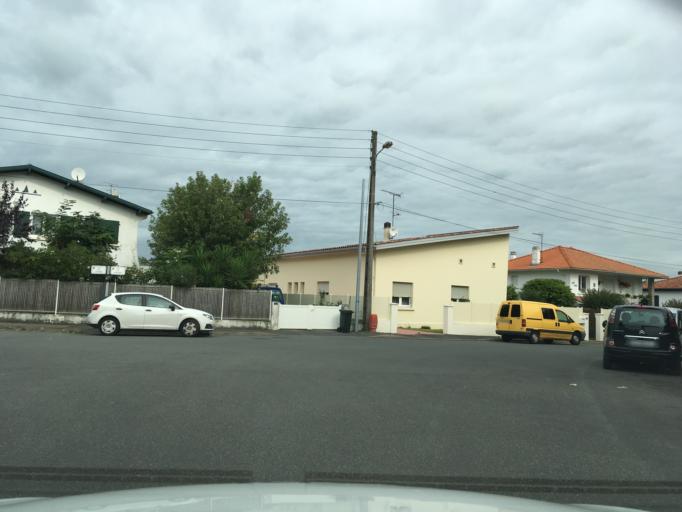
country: FR
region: Aquitaine
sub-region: Departement des Pyrenees-Atlantiques
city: Anglet
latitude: 43.4995
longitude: -1.5094
